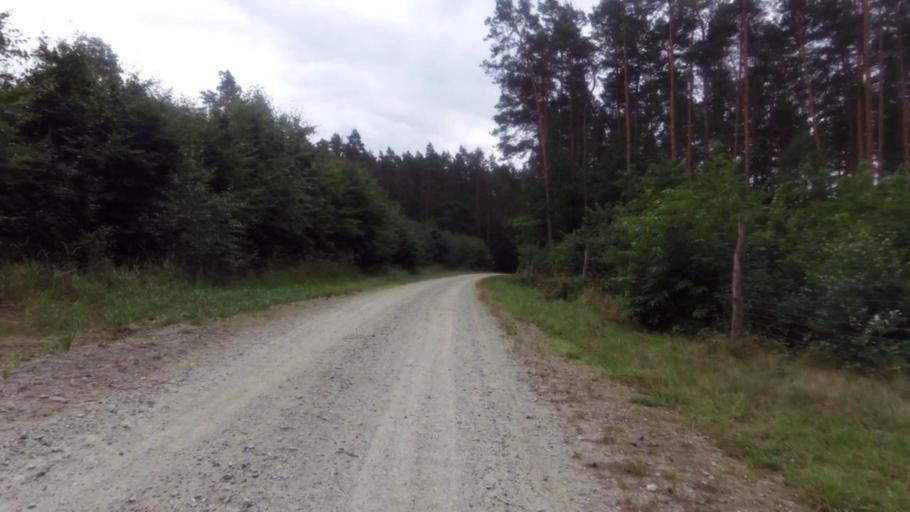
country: PL
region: Lubusz
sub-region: Powiat gorzowski
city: Kostrzyn nad Odra
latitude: 52.6454
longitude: 14.6425
